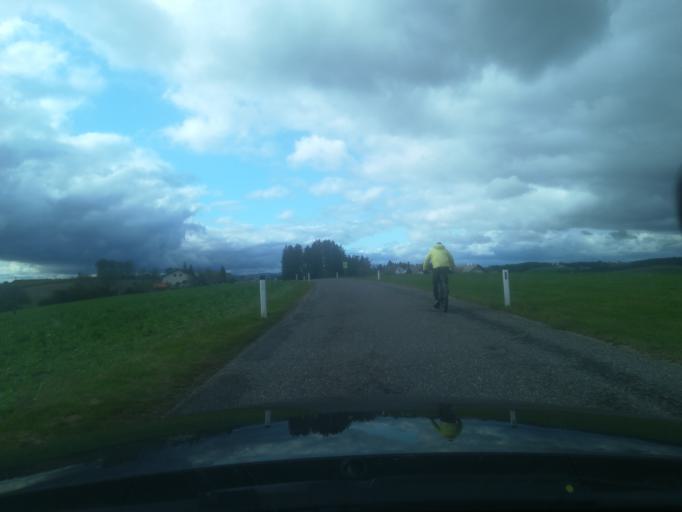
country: AT
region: Upper Austria
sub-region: Politischer Bezirk Urfahr-Umgebung
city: Herzogsdorf
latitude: 48.4223
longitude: 14.1531
